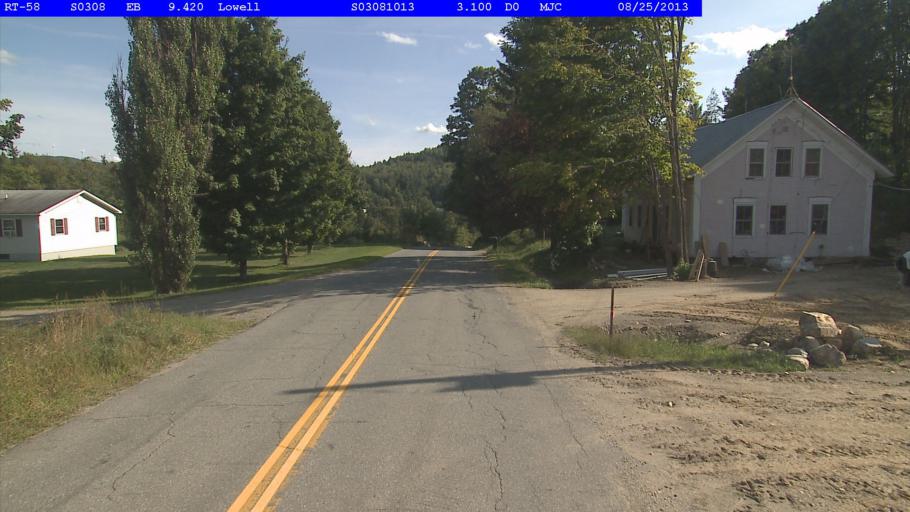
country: US
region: Vermont
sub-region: Lamoille County
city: Hyde Park
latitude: 44.8093
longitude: -72.4601
